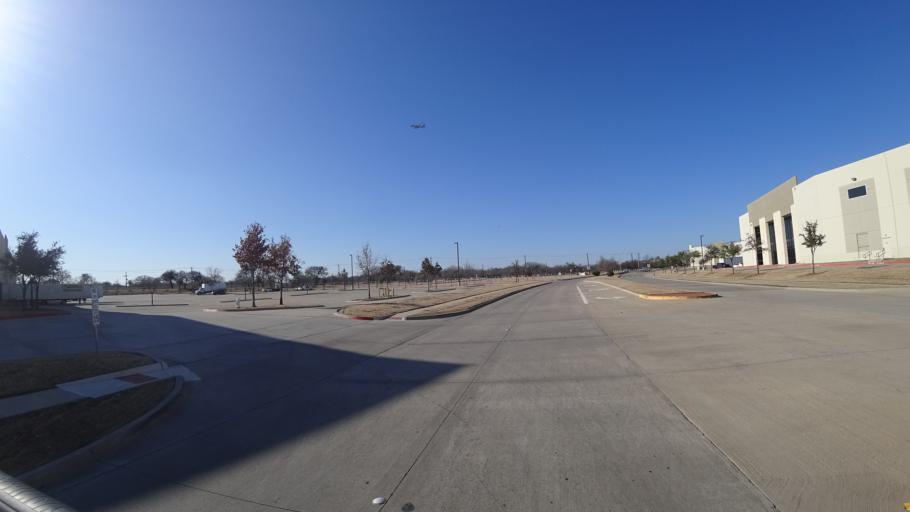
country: US
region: Texas
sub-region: Dallas County
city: Coppell
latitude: 32.9939
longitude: -97.0142
